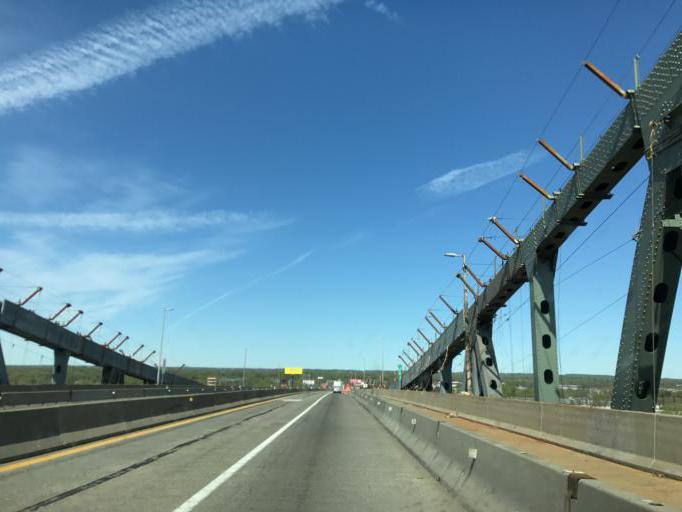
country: US
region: Pennsylvania
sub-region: Bucks County
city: Bristol
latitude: 40.1174
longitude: -74.8317
